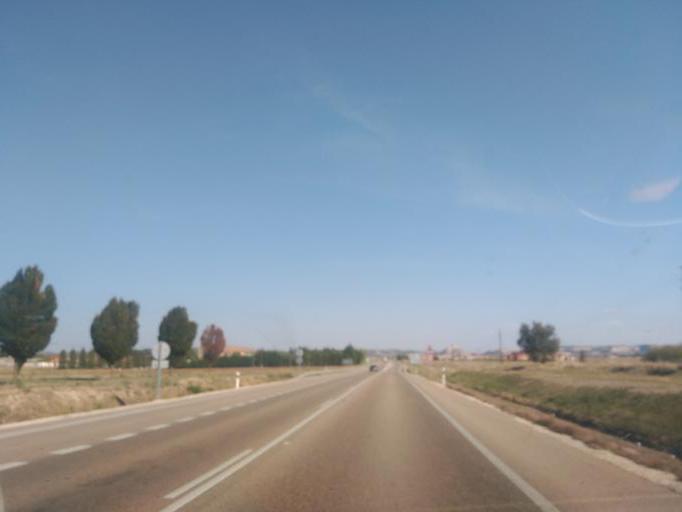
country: ES
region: Castille and Leon
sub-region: Provincia de Valladolid
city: Manzanillo
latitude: 41.6121
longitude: -4.1722
